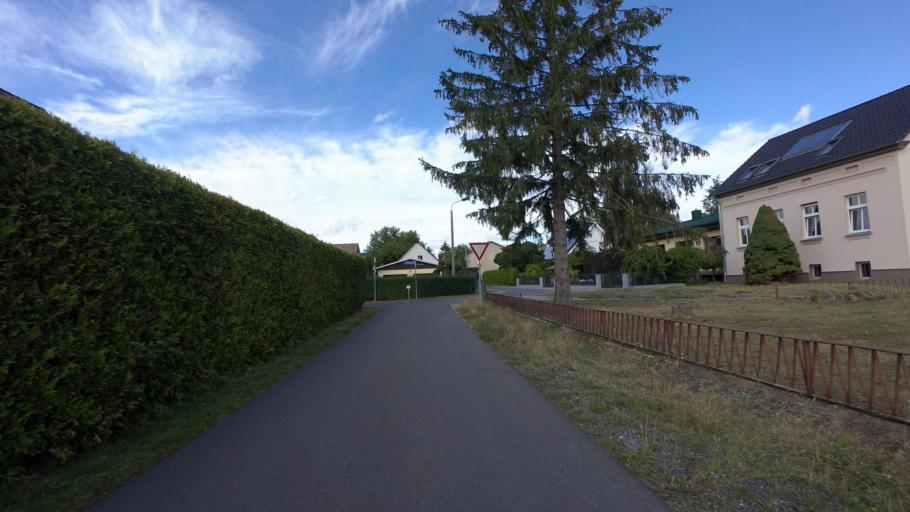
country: DE
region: Brandenburg
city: Werder
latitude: 52.3840
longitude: 12.8650
